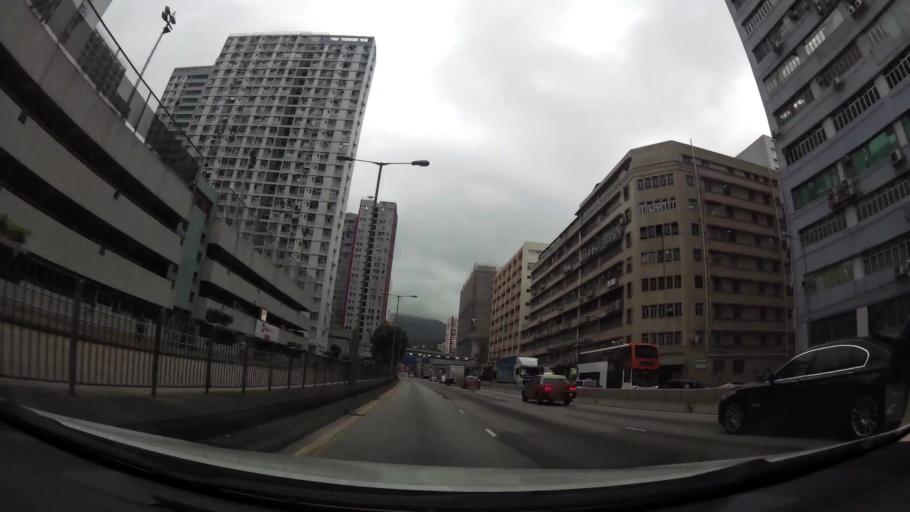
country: HK
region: Tsuen Wan
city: Tsuen Wan
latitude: 22.3653
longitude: 114.1329
